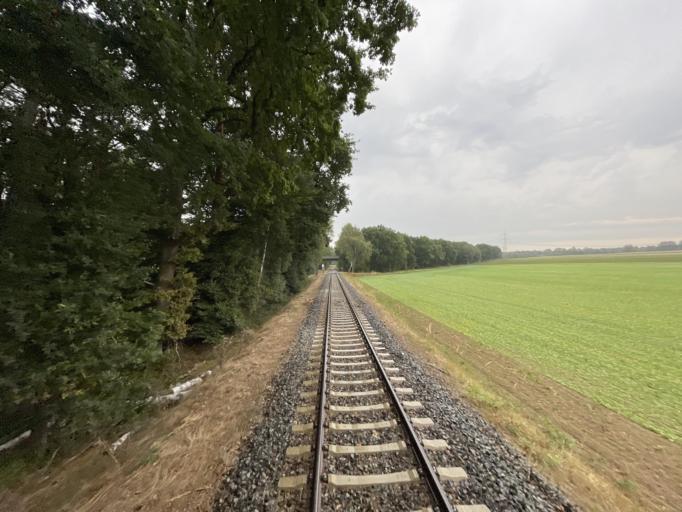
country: DE
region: Lower Saxony
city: Melbeck
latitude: 53.1948
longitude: 10.3779
